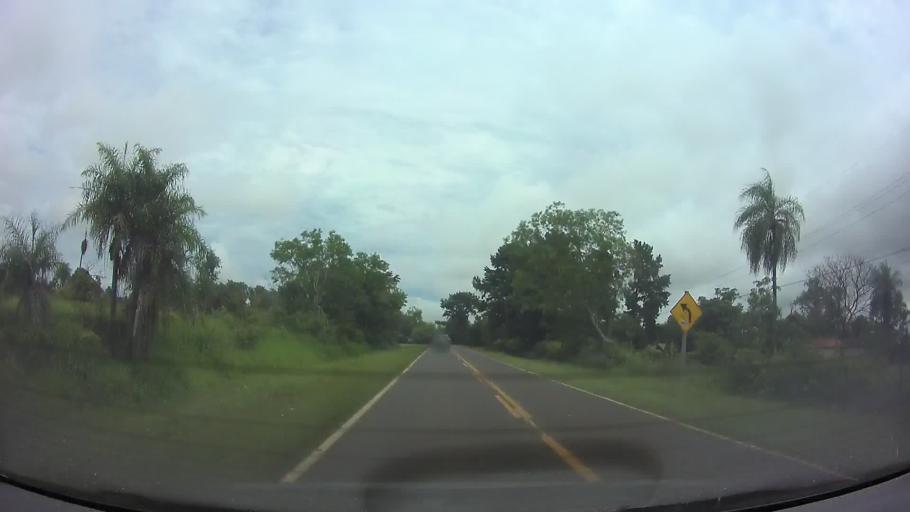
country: PY
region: Paraguari
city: Ybycui
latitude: -25.9924
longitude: -57.0545
